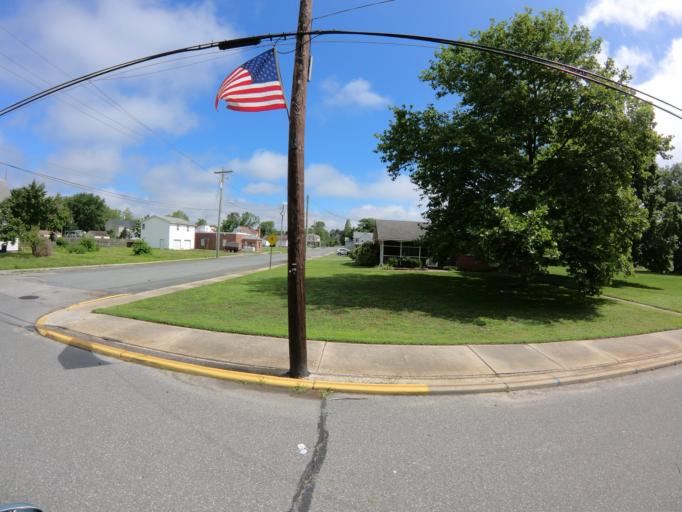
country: US
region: Delaware
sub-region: Kent County
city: Felton
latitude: 39.0078
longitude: -75.5732
